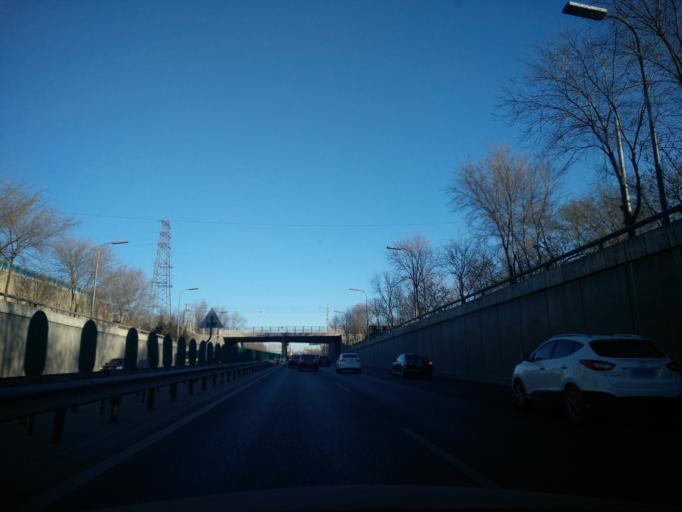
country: CN
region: Beijing
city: Lugu
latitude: 39.8511
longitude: 116.2150
